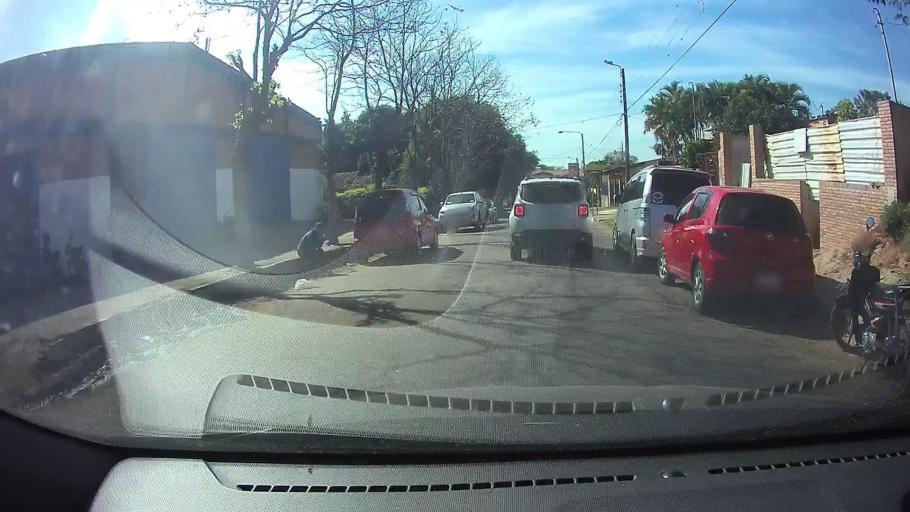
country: PY
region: Central
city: Villa Elisa
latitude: -25.3728
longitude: -57.5746
